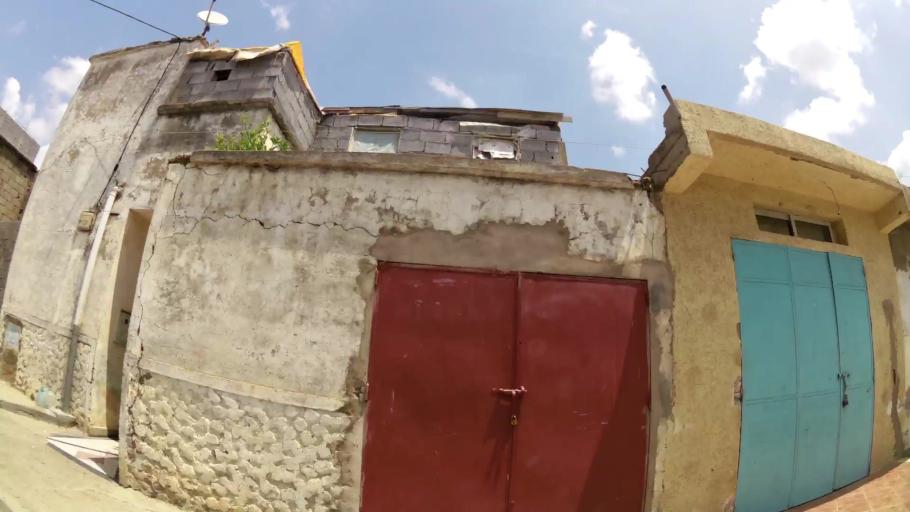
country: MA
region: Rabat-Sale-Zemmour-Zaer
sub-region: Khemisset
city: Tiflet
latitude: 34.0024
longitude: -6.5307
